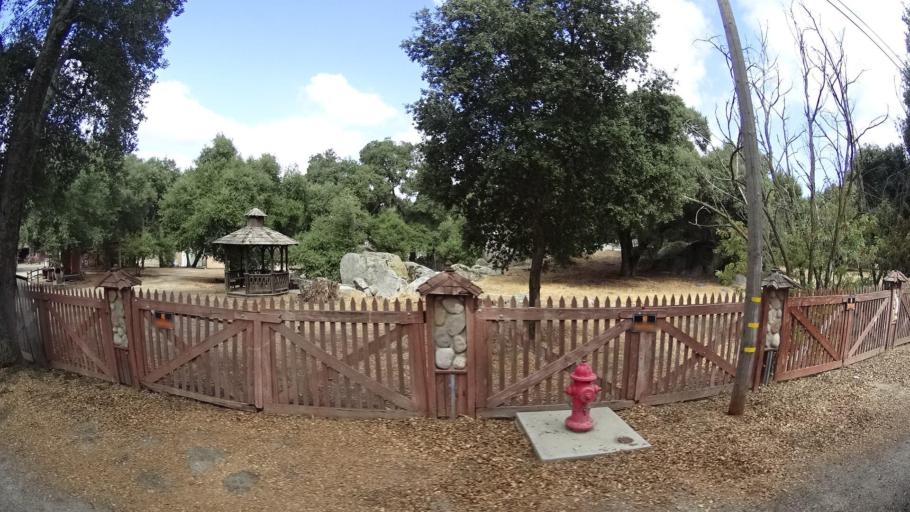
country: US
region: California
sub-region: San Diego County
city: Campo
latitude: 32.6817
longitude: -116.5145
